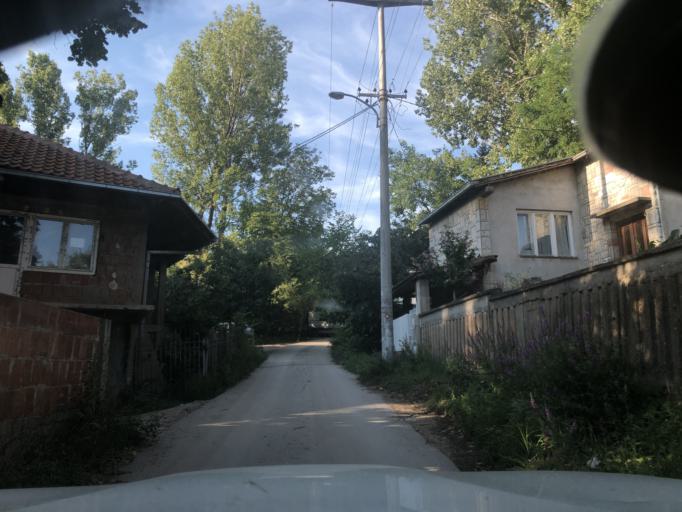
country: RS
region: Central Serbia
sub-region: Nisavski Okrug
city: Nis
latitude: 43.3223
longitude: 21.9518
